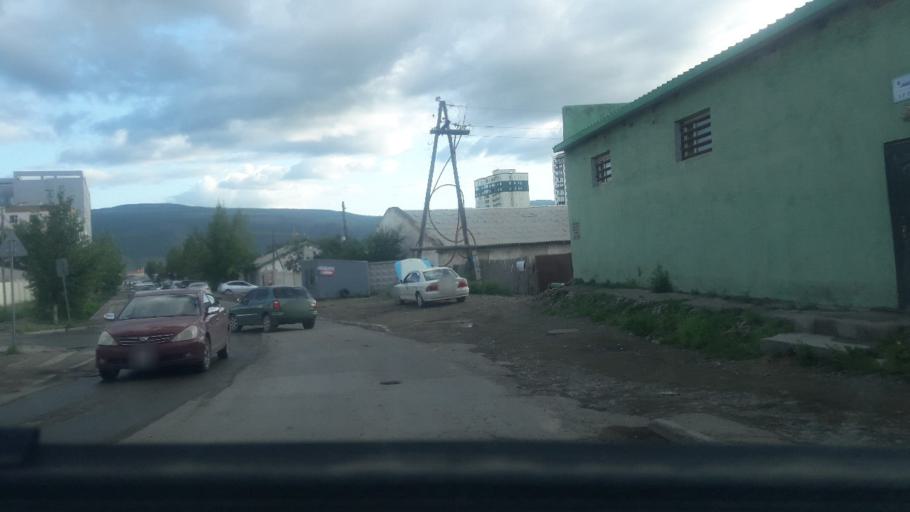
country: MN
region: Ulaanbaatar
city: Ulaanbaatar
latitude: 47.9171
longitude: 106.9945
